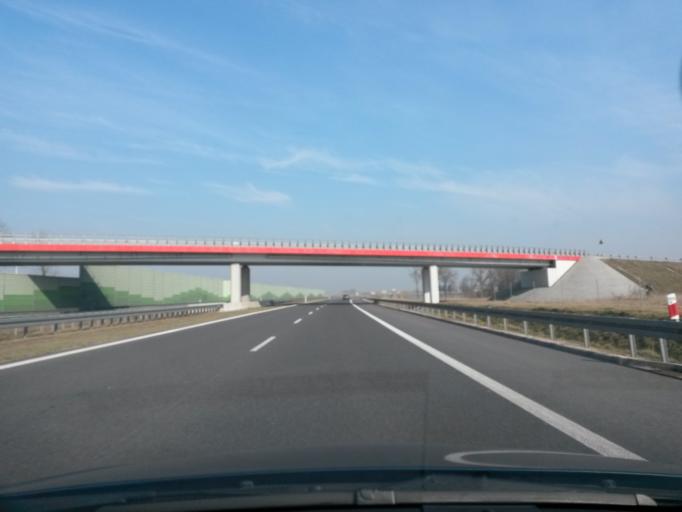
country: PL
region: Lodz Voivodeship
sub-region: Powiat kutnowski
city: Krzyzanow
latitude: 52.1470
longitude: 19.4819
